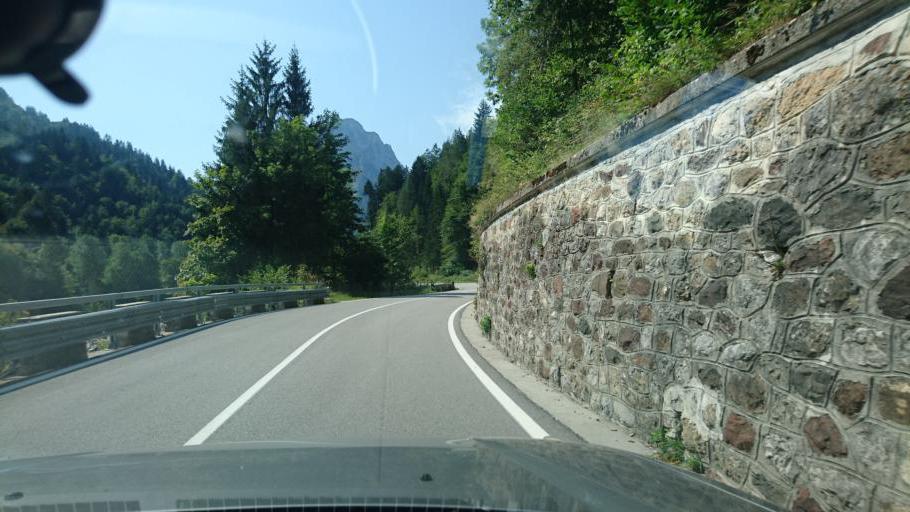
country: IT
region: Friuli Venezia Giulia
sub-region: Provincia di Udine
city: Tarvisio
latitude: 46.4858
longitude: 13.5809
